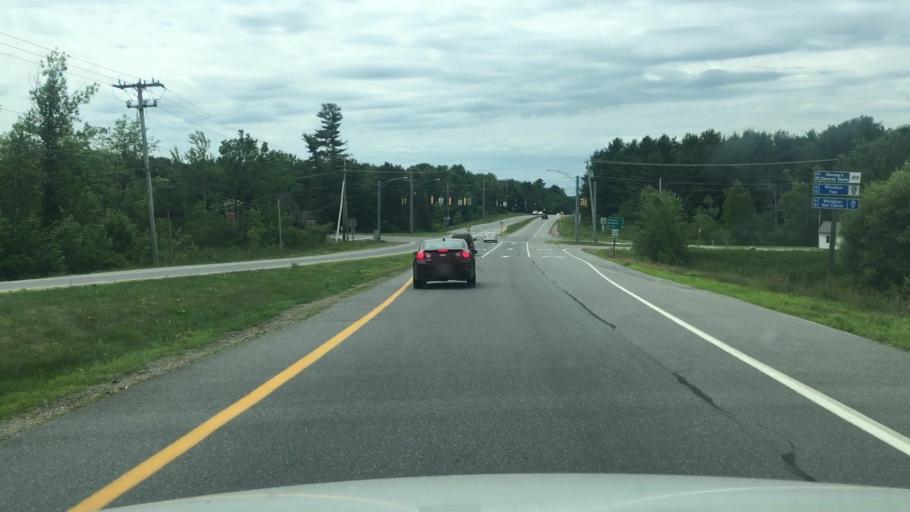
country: US
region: Maine
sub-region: Kennebec County
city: Windsor
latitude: 44.3956
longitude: -69.5696
